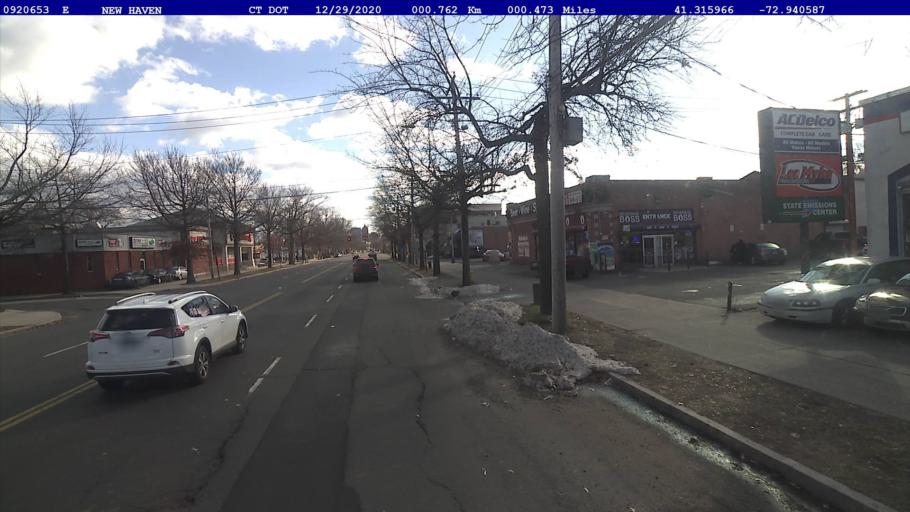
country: US
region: Connecticut
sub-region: New Haven County
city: New Haven
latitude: 41.3160
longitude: -72.9406
